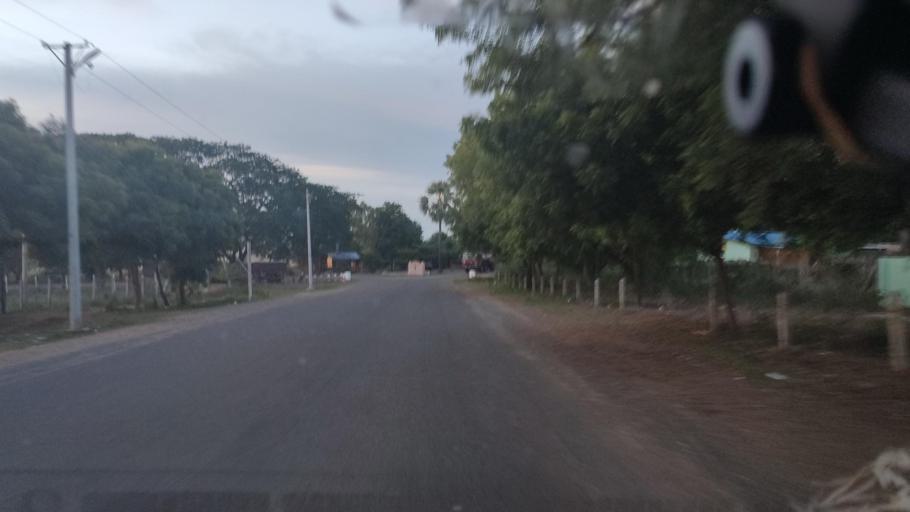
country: MM
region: Magway
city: Magway
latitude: 20.1828
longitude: 94.9935
